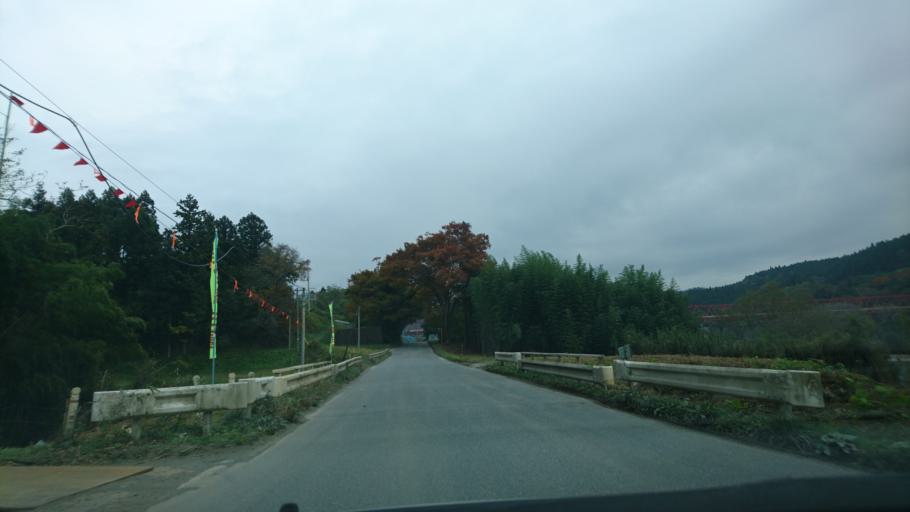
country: JP
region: Iwate
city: Ichinoseki
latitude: 38.9515
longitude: 141.1772
